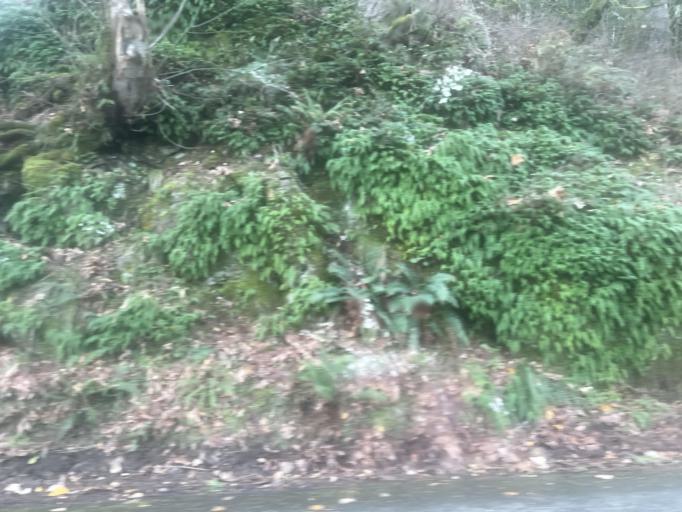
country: US
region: Washington
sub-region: Clark County
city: Washougal
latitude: 45.5396
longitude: -122.2155
